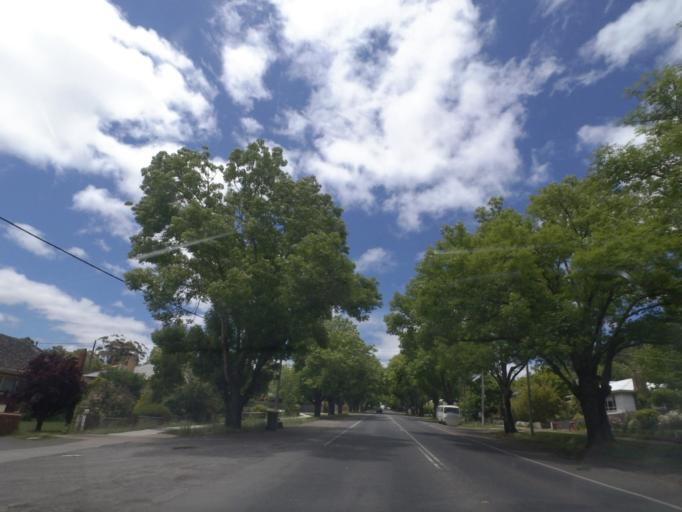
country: AU
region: Victoria
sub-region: Mount Alexander
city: Castlemaine
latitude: -37.3398
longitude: 144.1467
